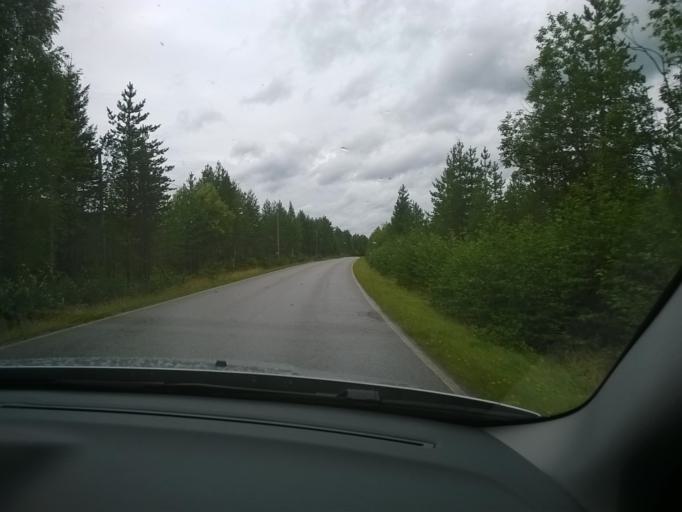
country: FI
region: Kainuu
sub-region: Kehys-Kainuu
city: Kuhmo
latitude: 64.1281
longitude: 29.4587
